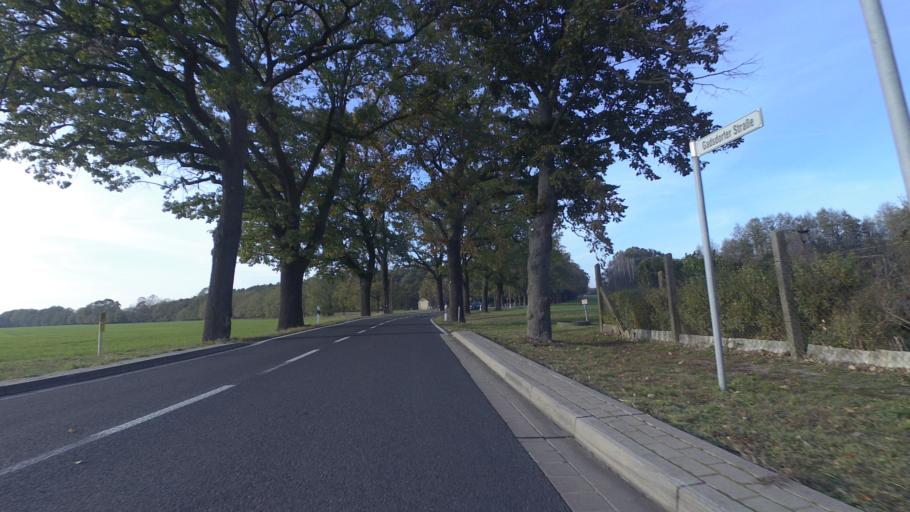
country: DE
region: Brandenburg
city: Sperenberg
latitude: 52.1910
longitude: 13.3206
